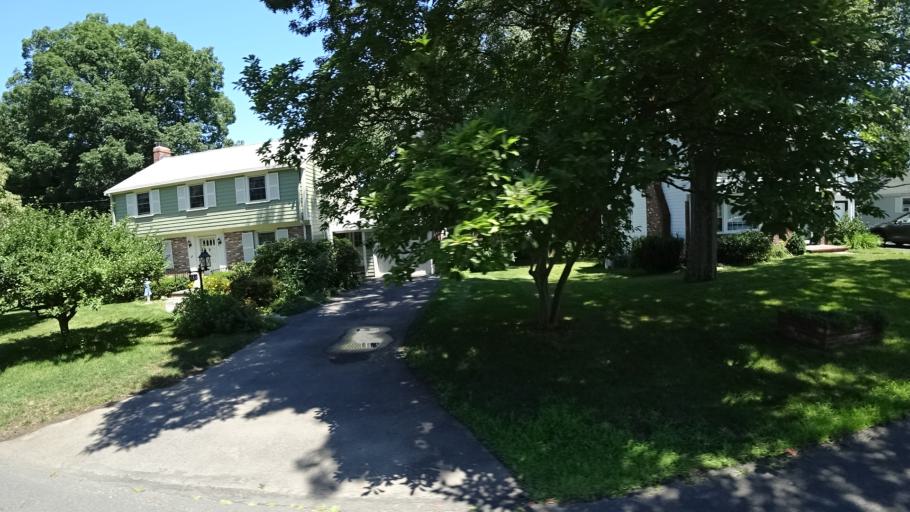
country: US
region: Massachusetts
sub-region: Norfolk County
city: Dedham
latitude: 42.2305
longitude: -71.1880
